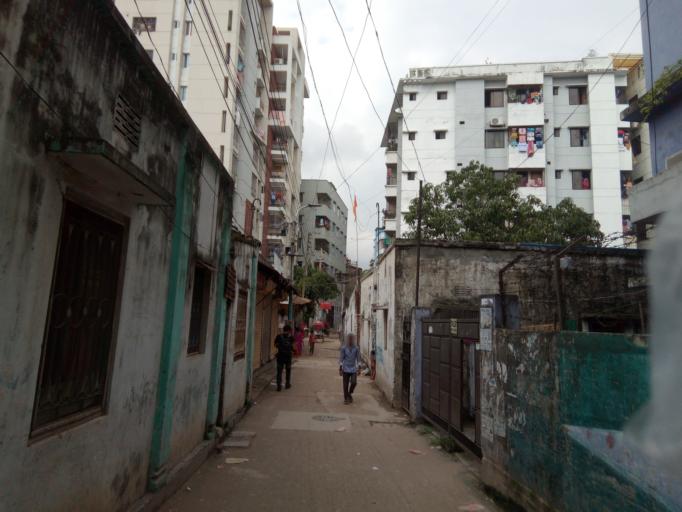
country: BD
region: Dhaka
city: Azimpur
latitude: 23.7423
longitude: 90.3677
